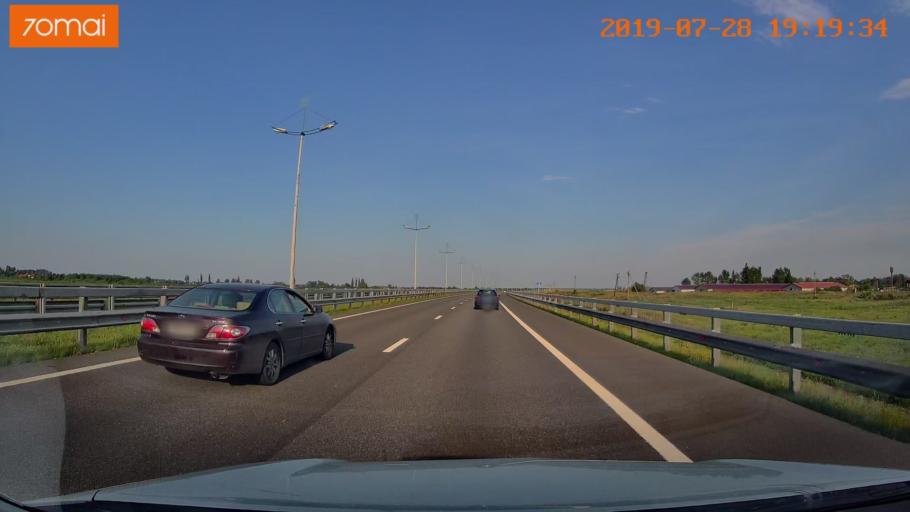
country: RU
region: Kaliningrad
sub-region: Zelenogradskiy Rayon
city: Zelenogradsk
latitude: 54.9199
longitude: 20.4631
